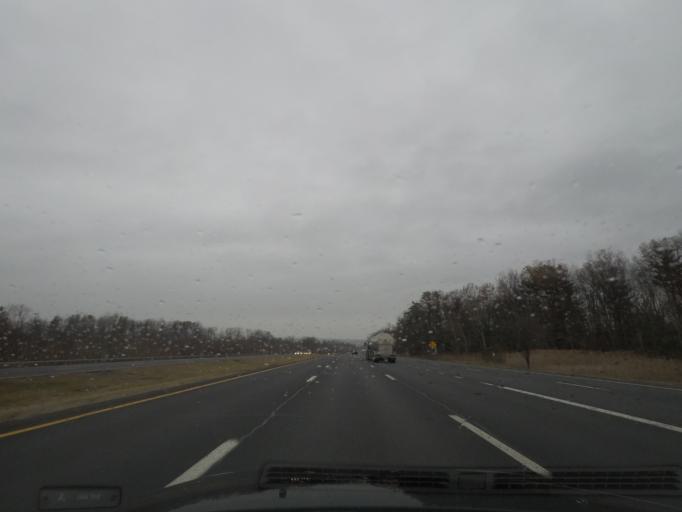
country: US
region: New York
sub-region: Rensselaer County
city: Rensselaer
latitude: 42.6520
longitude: -73.7152
